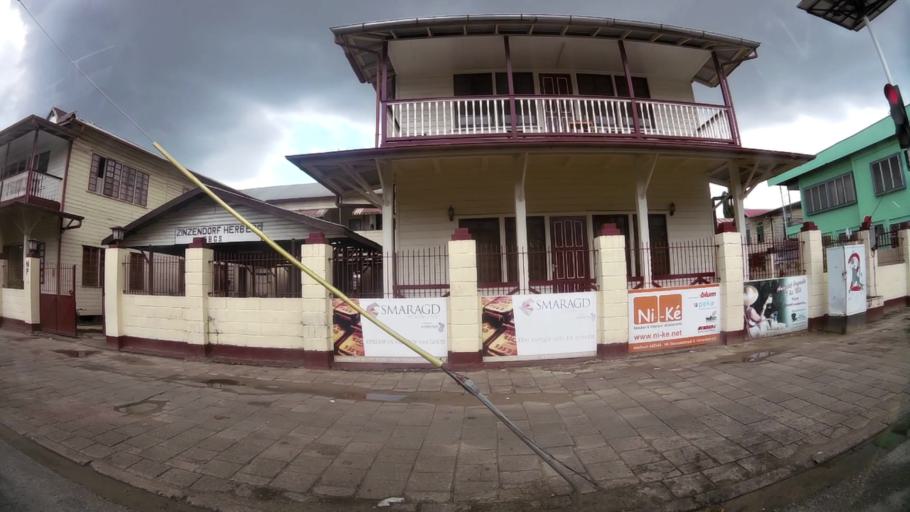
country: SR
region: Paramaribo
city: Paramaribo
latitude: 5.8312
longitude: -55.1592
